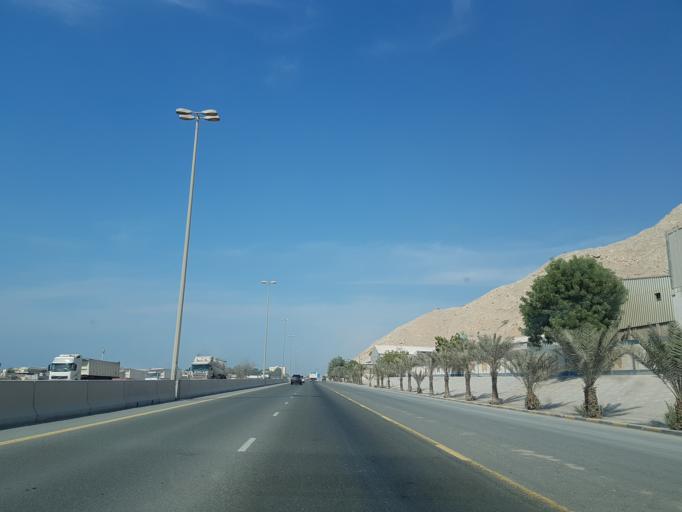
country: AE
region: Ra's al Khaymah
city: Ras al-Khaimah
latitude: 25.8550
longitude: 56.0207
